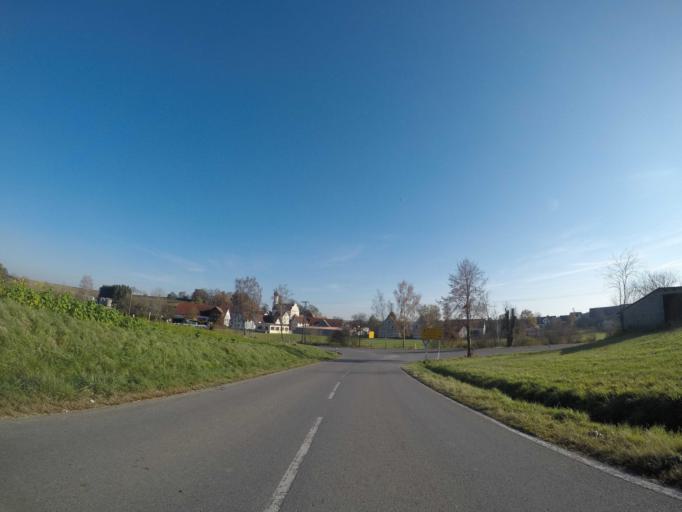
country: DE
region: Baden-Wuerttemberg
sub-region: Tuebingen Region
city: Grundsheim
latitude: 48.1795
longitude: 9.6650
